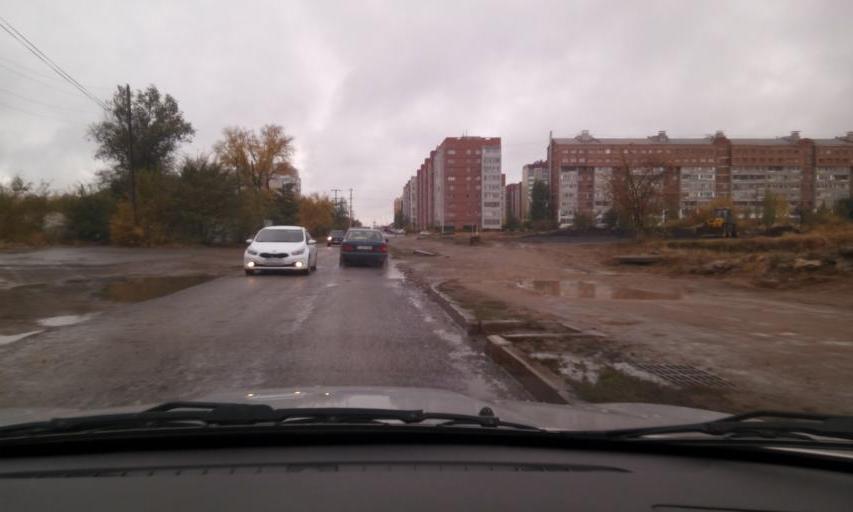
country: KZ
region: Astana Qalasy
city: Astana
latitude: 51.1633
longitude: 71.4005
